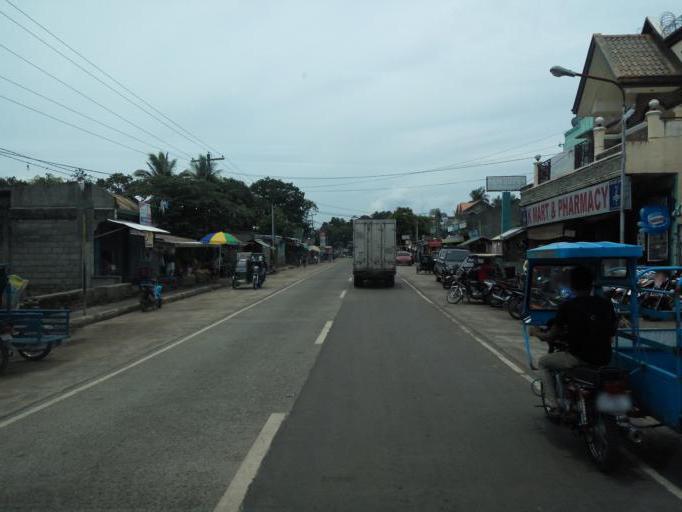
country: PH
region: Cagayan Valley
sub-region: Province of Quirino
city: Diffun
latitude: 16.5934
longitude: 121.5024
